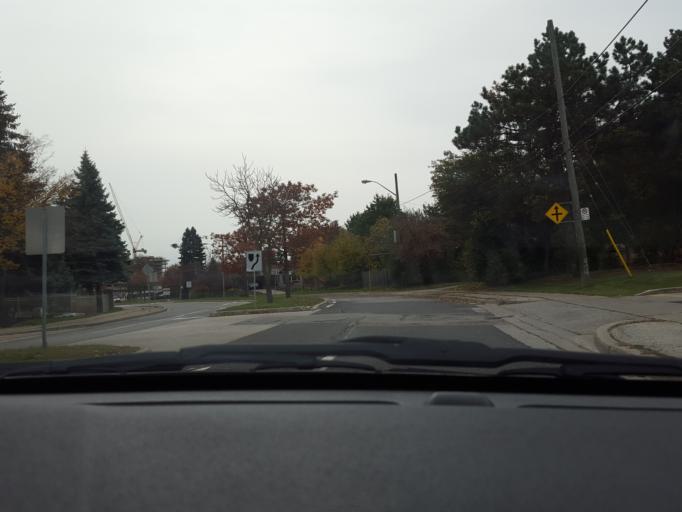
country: CA
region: Ontario
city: Willowdale
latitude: 43.7385
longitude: -79.3471
